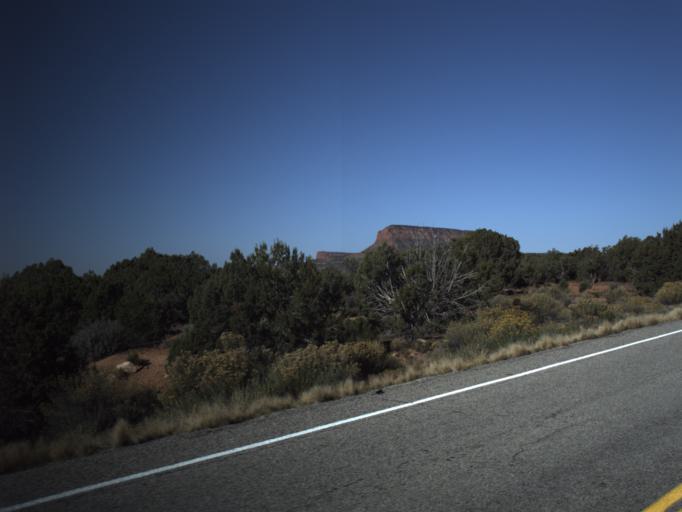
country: US
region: Utah
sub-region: San Juan County
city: Blanding
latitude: 37.5454
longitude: -109.9834
